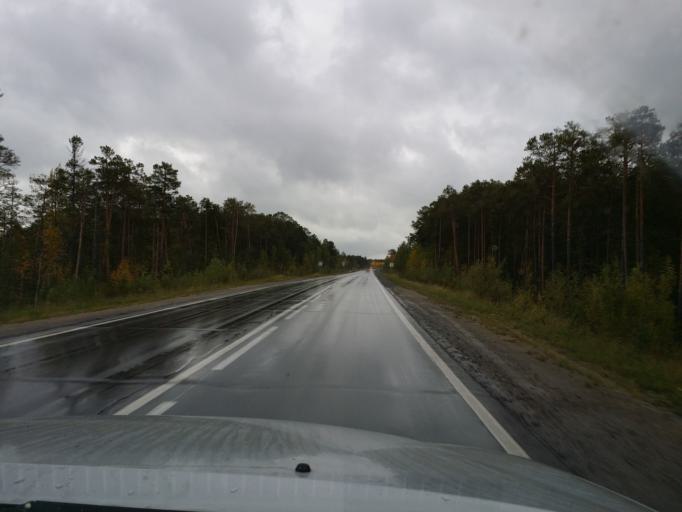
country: RU
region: Khanty-Mansiyskiy Avtonomnyy Okrug
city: Megion
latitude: 61.1214
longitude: 75.8340
